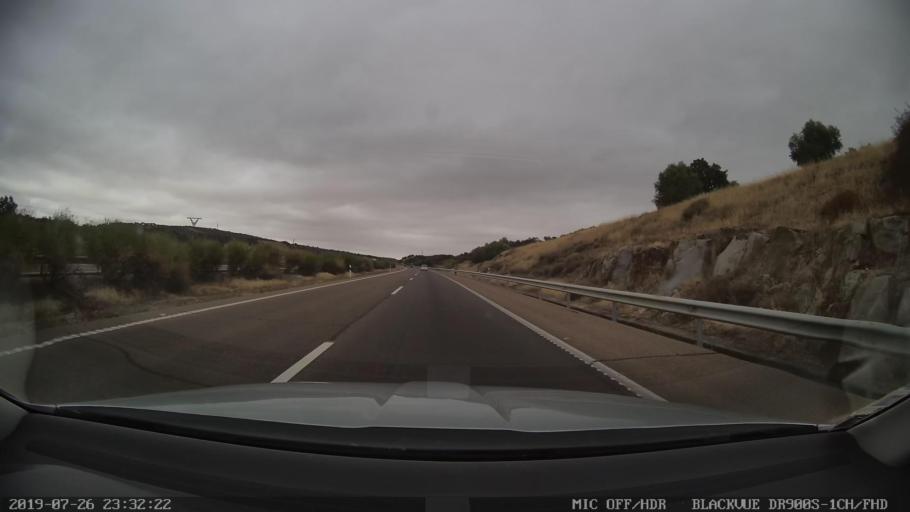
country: ES
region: Extremadura
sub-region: Provincia de Caceres
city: Puerto de Santa Cruz
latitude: 39.3176
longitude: -5.8563
